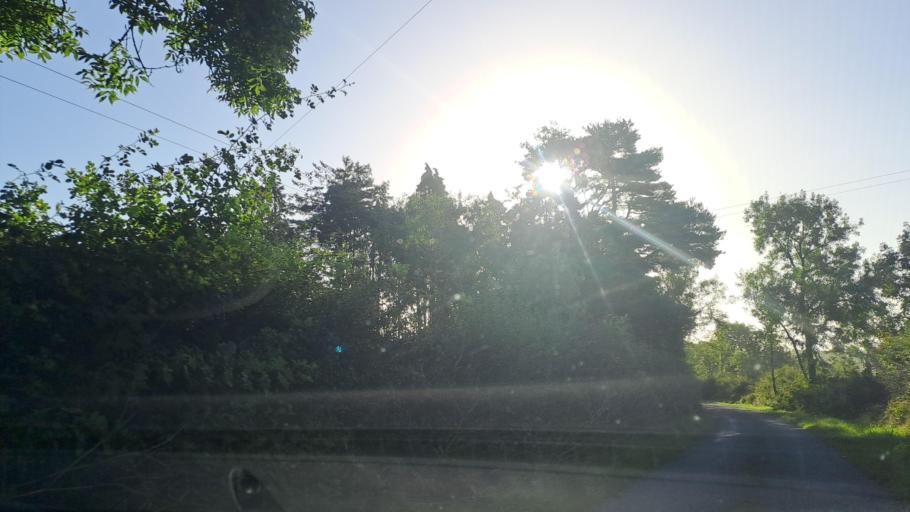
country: IE
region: Ulster
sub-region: An Cabhan
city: Kingscourt
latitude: 53.9807
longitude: -6.8519
